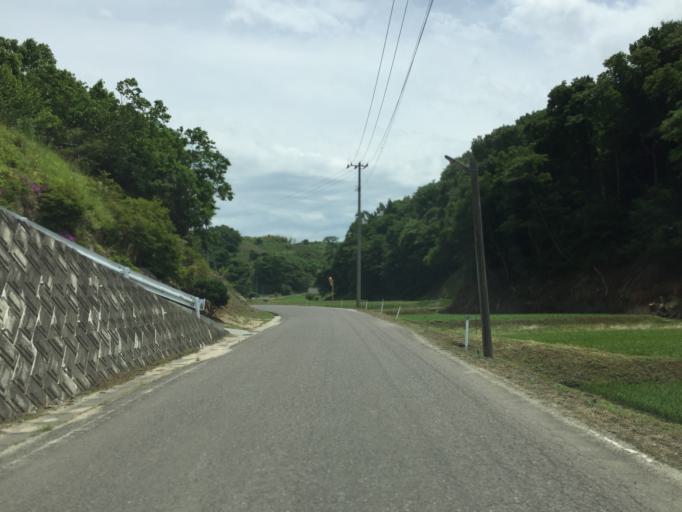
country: JP
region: Fukushima
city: Miharu
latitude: 37.4134
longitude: 140.5177
